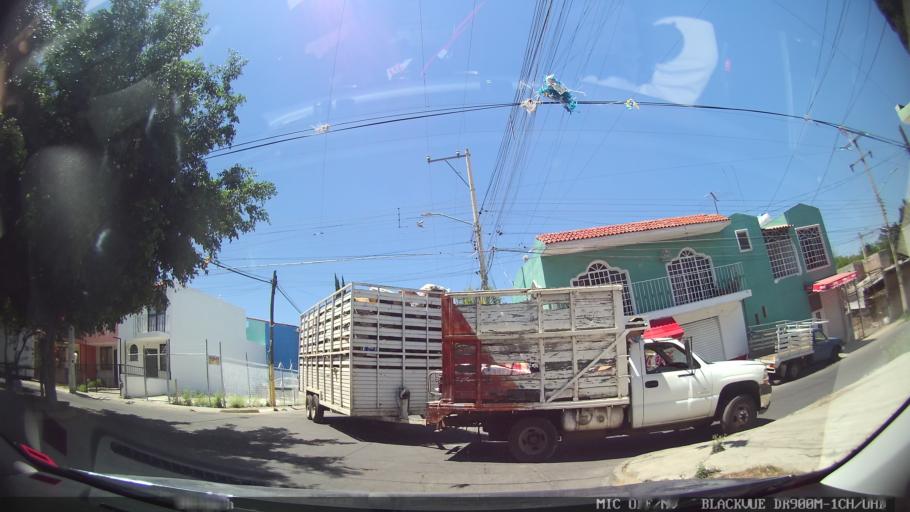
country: MX
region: Jalisco
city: Tlaquepaque
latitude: 20.6620
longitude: -103.2722
